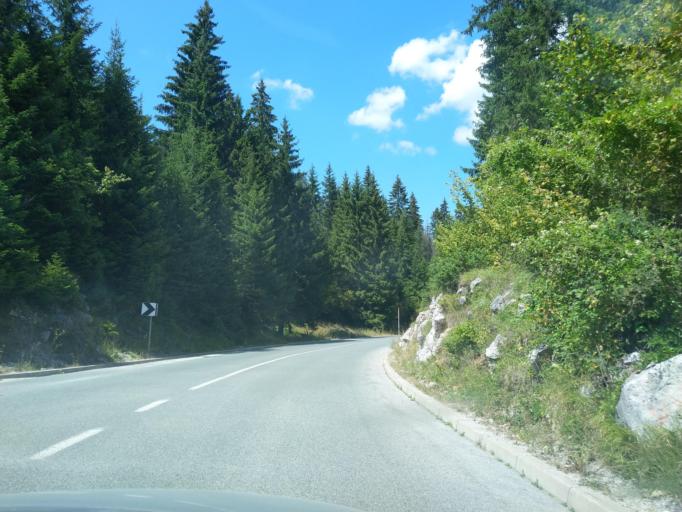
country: RS
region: Central Serbia
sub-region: Zlatiborski Okrug
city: Nova Varos
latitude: 43.3931
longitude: 19.8460
